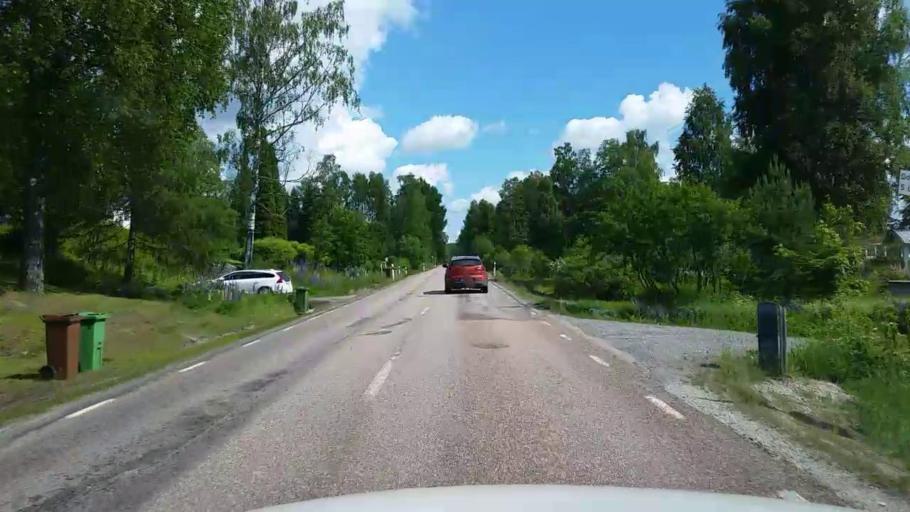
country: SE
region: Vaestmanland
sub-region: Skinnskattebergs Kommun
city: Skinnskatteberg
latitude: 59.7565
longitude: 15.8178
